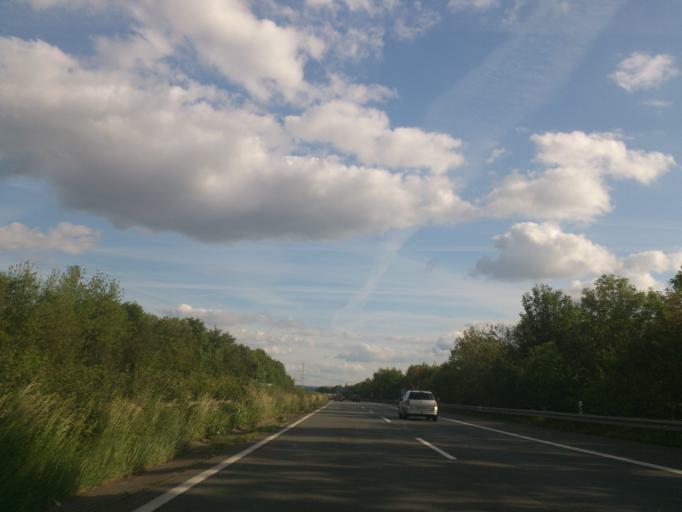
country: DE
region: North Rhine-Westphalia
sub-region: Regierungsbezirk Detmold
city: Paderborn
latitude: 51.7129
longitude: 8.7047
